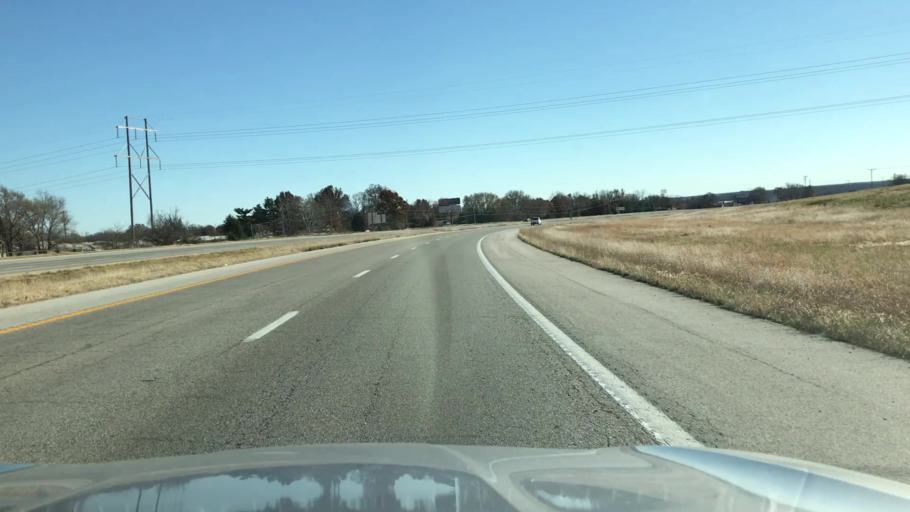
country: US
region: Missouri
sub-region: Jasper County
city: Carthage
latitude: 37.1320
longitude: -94.3128
